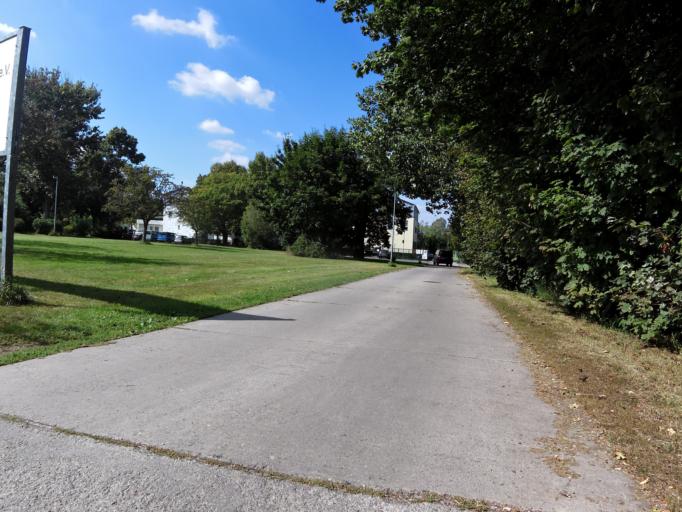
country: DE
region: Saxony
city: Leipzig
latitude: 51.3649
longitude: 12.4196
